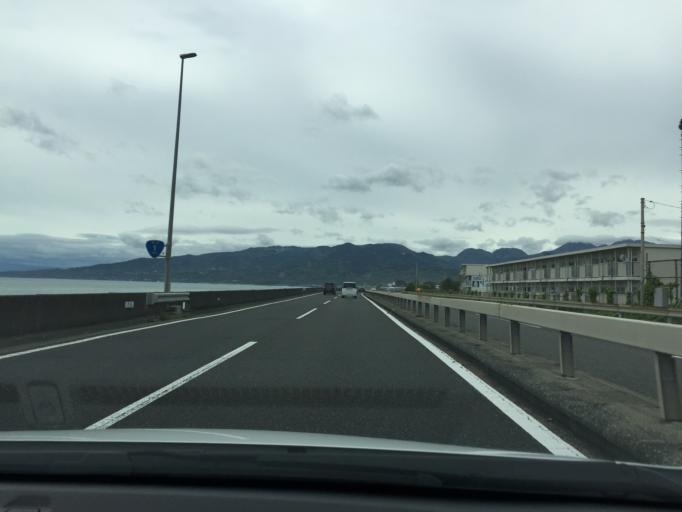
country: JP
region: Kanagawa
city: Odawara
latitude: 35.2655
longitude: 139.1918
